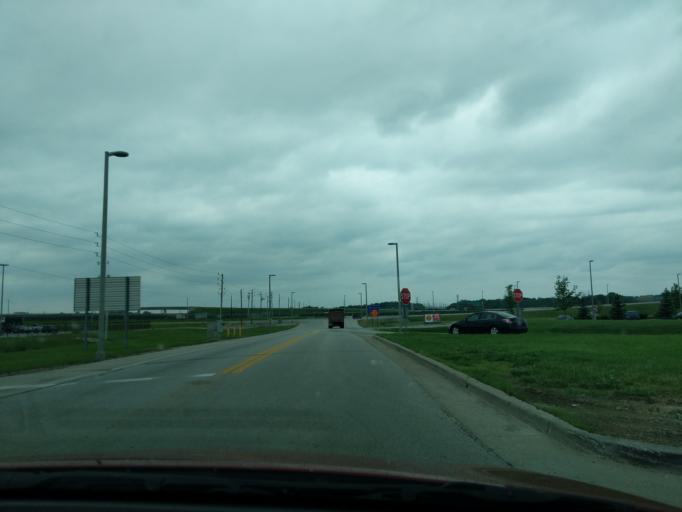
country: US
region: Indiana
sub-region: Hendricks County
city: Plainfield
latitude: 39.6996
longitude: -86.3129
